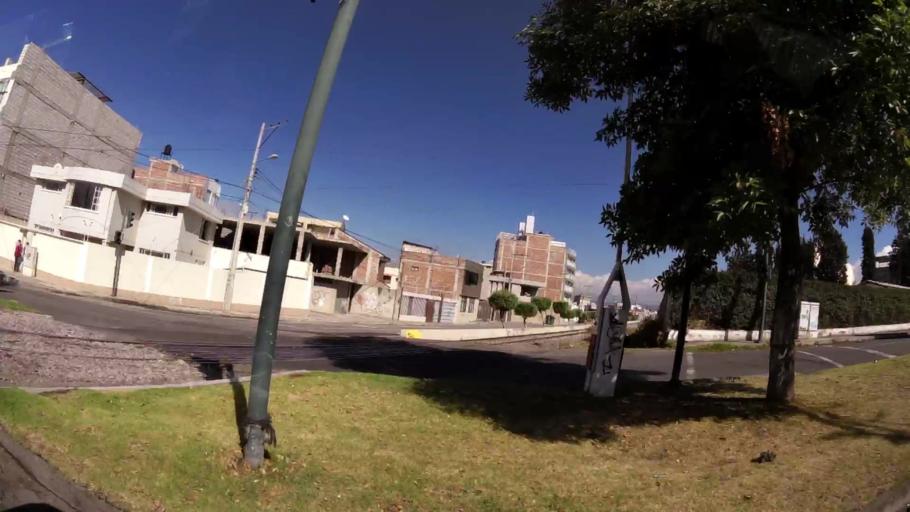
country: EC
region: Chimborazo
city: Riobamba
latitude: -1.6591
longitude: -78.6682
